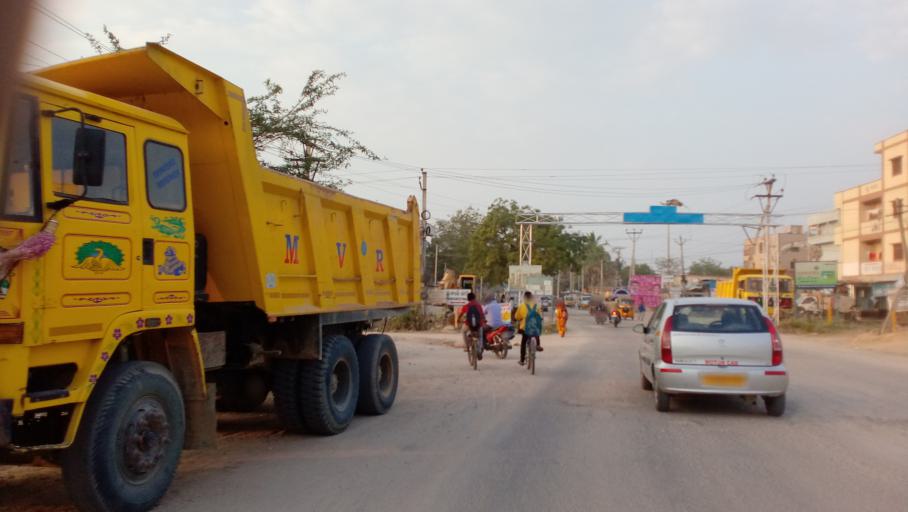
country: IN
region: Telangana
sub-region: Medak
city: Serilingampalle
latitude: 17.5082
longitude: 78.3184
